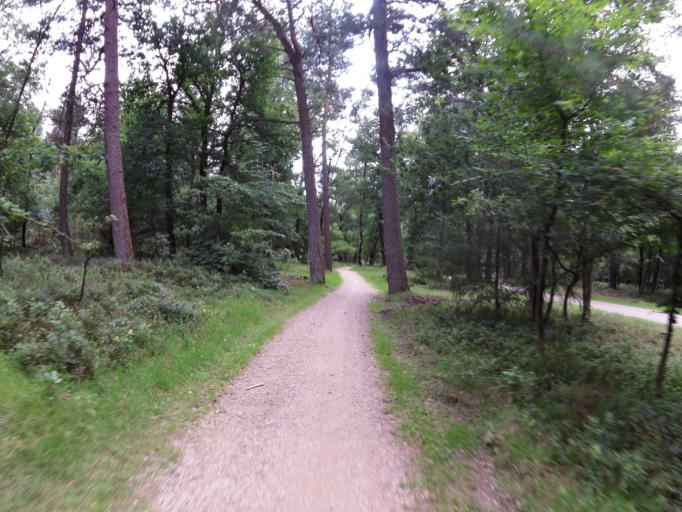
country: NL
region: Gelderland
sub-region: Gemeente Apeldoorn
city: Loenen
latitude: 52.0914
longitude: 5.9901
